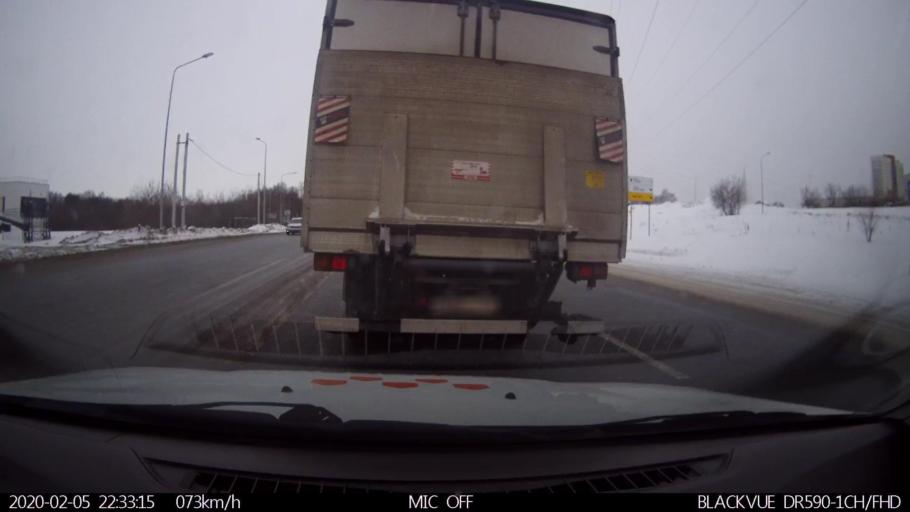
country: RU
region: Nizjnij Novgorod
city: Imeni Stepana Razina
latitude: 54.7365
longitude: 44.2067
